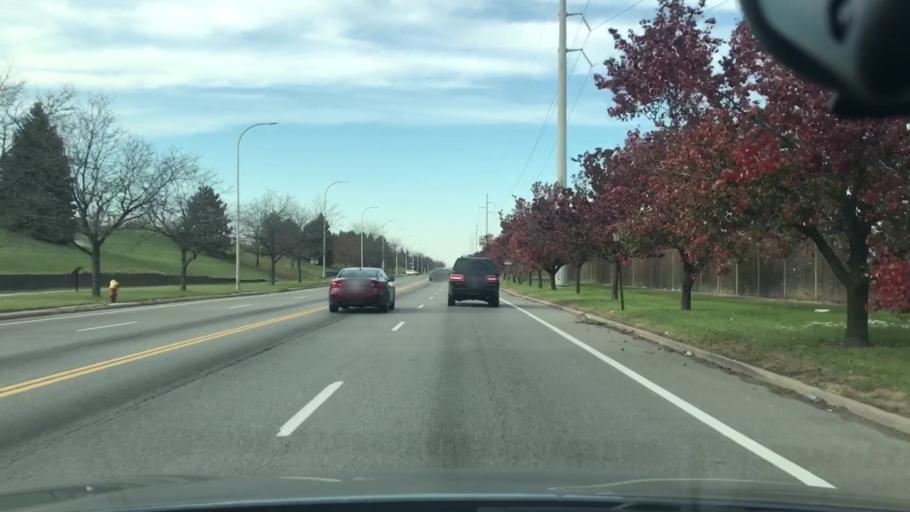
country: US
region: Michigan
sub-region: Wayne County
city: Grosse Pointe Park
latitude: 42.3719
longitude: -82.9738
